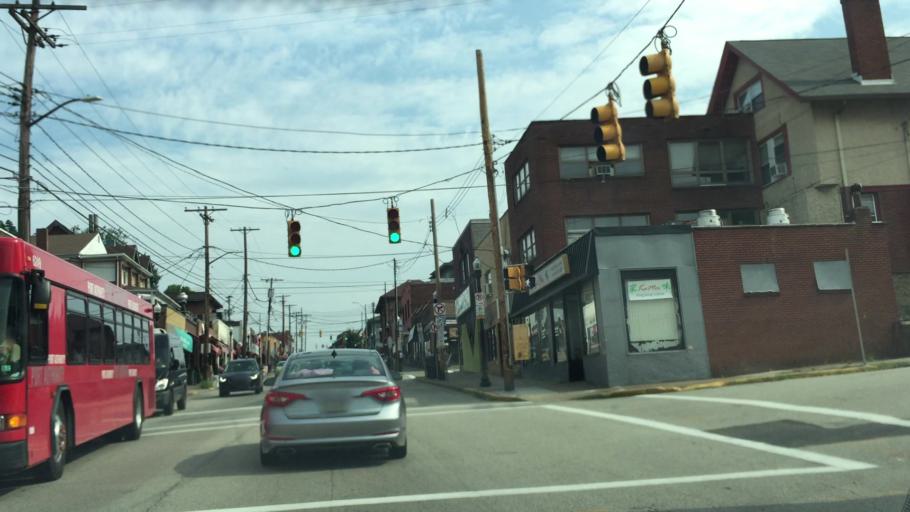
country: US
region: Pennsylvania
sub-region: Allegheny County
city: Homestead
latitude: 40.4322
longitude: -79.9231
